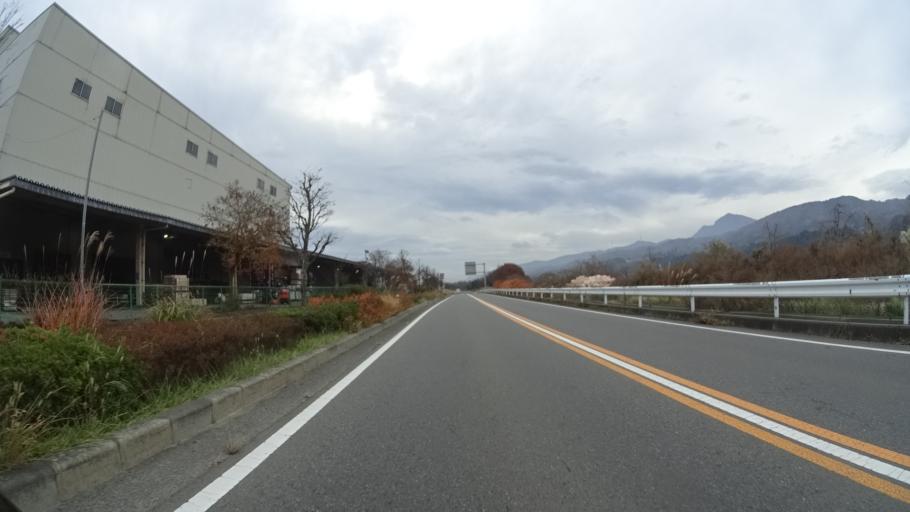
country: JP
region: Gunma
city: Numata
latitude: 36.6545
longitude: 139.0216
